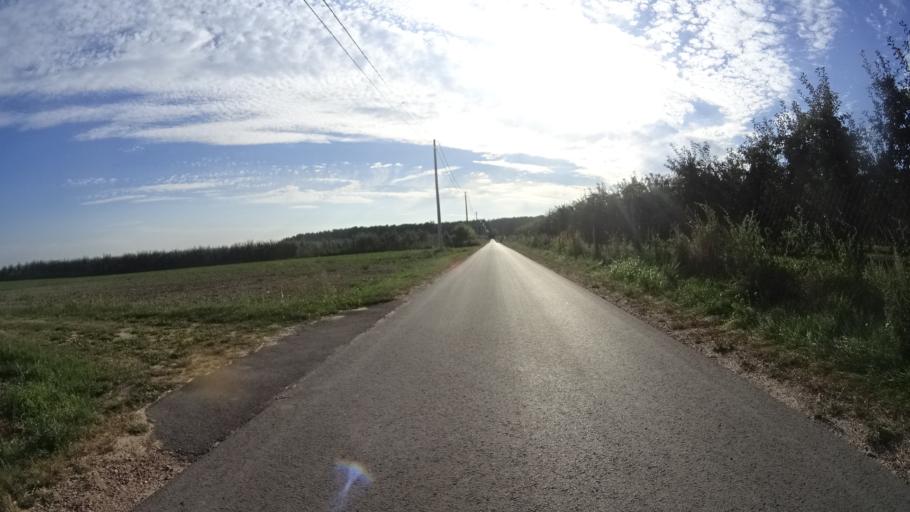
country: PL
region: Masovian Voivodeship
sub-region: Powiat bialobrzeski
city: Wysmierzyce
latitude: 51.6768
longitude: 20.8162
